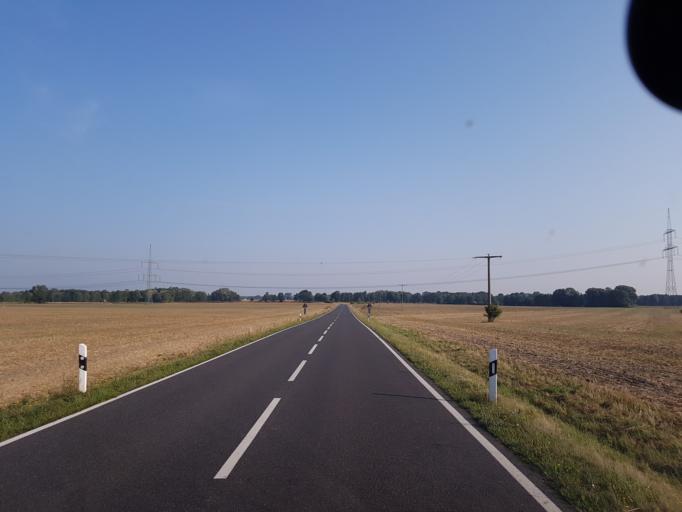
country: DE
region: Brandenburg
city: Finsterwalde
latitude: 51.6486
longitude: 13.7349
